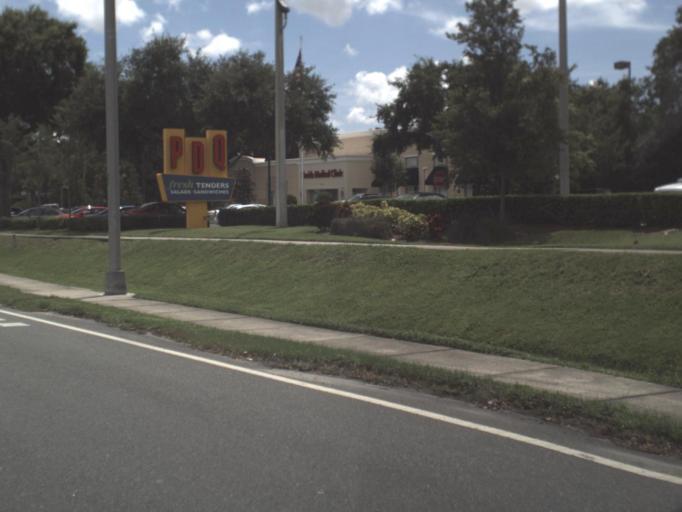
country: US
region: Florida
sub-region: Hillsborough County
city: Carrollwood
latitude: 28.0619
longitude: -82.5040
